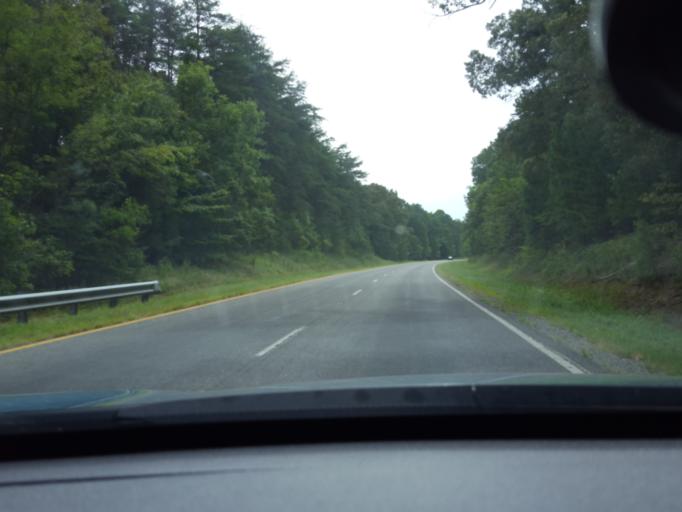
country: US
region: Virginia
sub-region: Caroline County
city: Bowling Green
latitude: 38.1251
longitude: -77.2453
